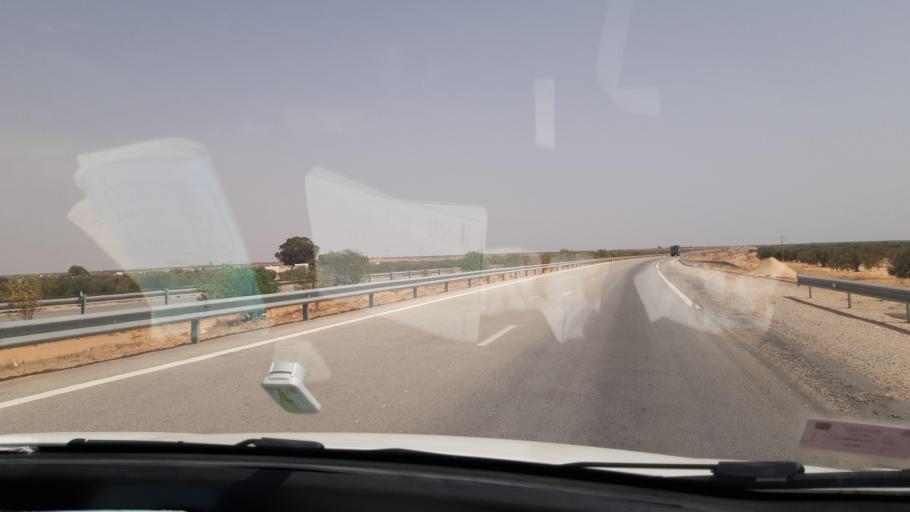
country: TN
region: Safaqis
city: Bi'r `Ali Bin Khalifah
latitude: 34.5263
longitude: 10.1313
